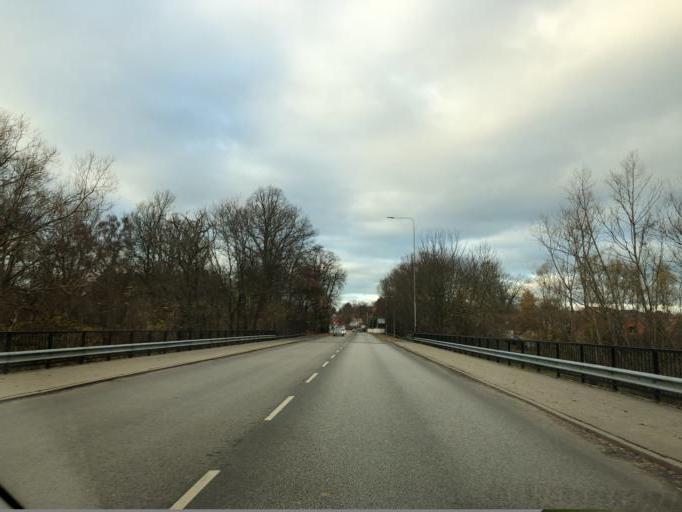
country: SE
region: Skane
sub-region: Kavlinge Kommun
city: Kaevlinge
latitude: 55.7867
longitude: 13.1076
